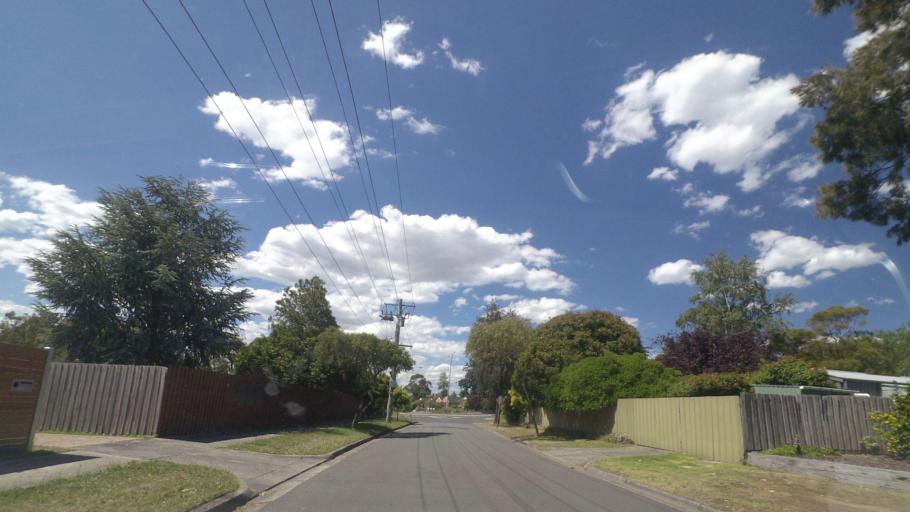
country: AU
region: Victoria
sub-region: Yarra Ranges
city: Kilsyth
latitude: -37.8078
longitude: 145.3249
